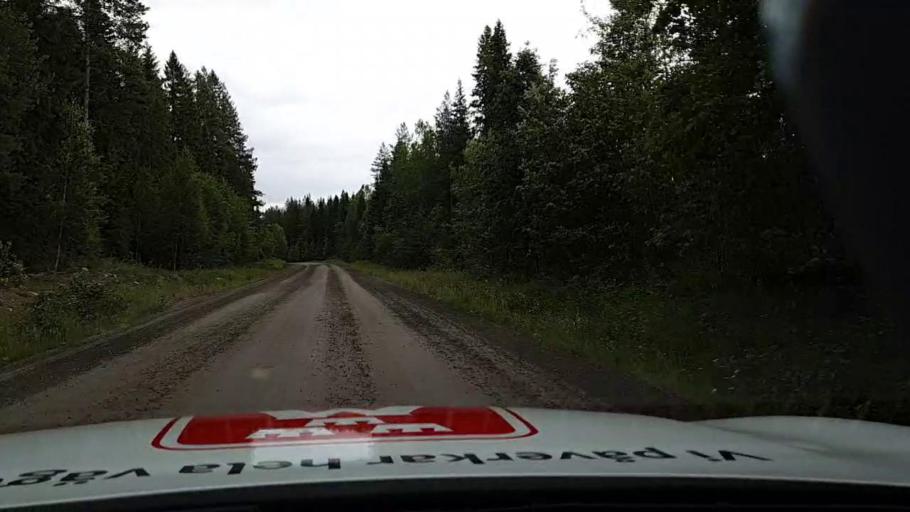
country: SE
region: Vaesternorrland
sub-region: Solleftea Kommun
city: As
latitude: 63.5094
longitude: 16.4092
